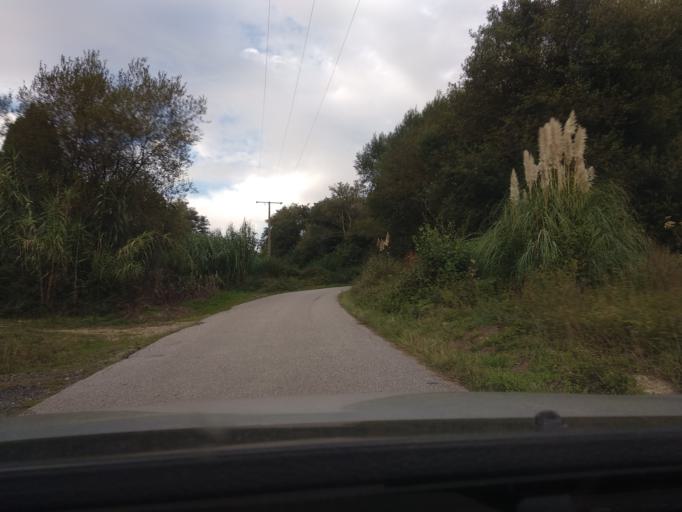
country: ES
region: Galicia
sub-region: Provincia de Pontevedra
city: Moana
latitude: 42.2945
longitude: -8.7356
